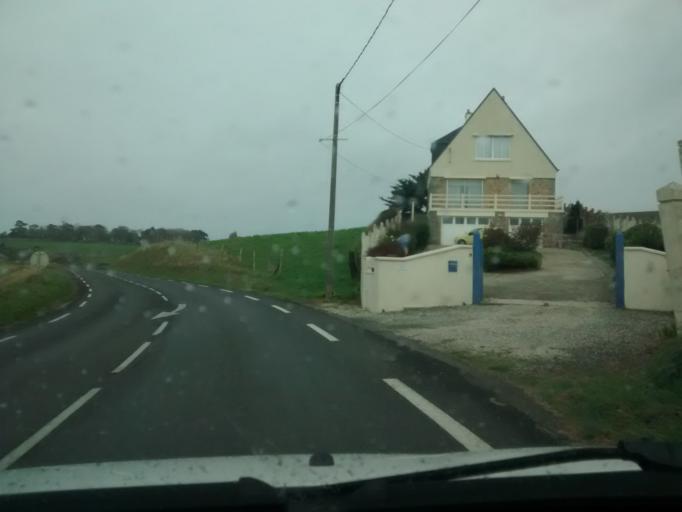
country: FR
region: Lower Normandy
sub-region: Departement de la Manche
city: Saint-Pair-sur-Mer
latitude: 48.8236
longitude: -1.5752
